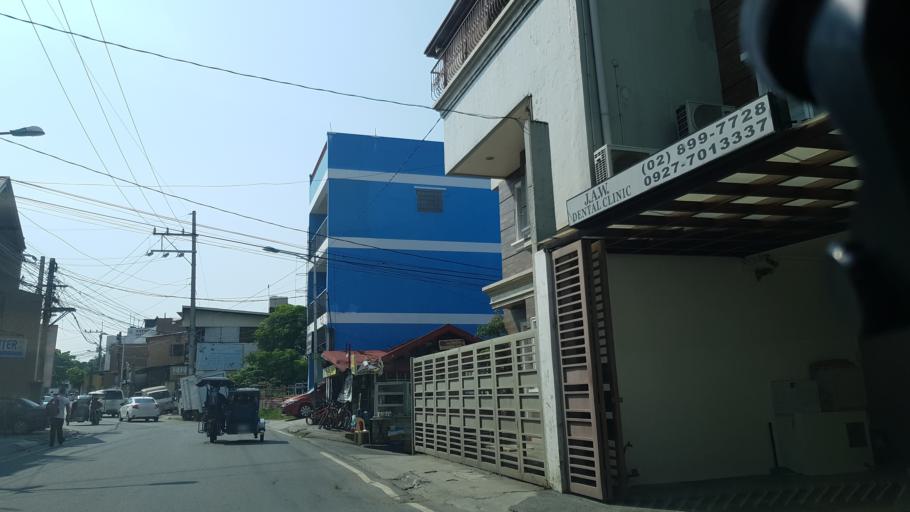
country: PH
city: Sambayanihan People's Village
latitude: 14.4874
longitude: 121.0258
